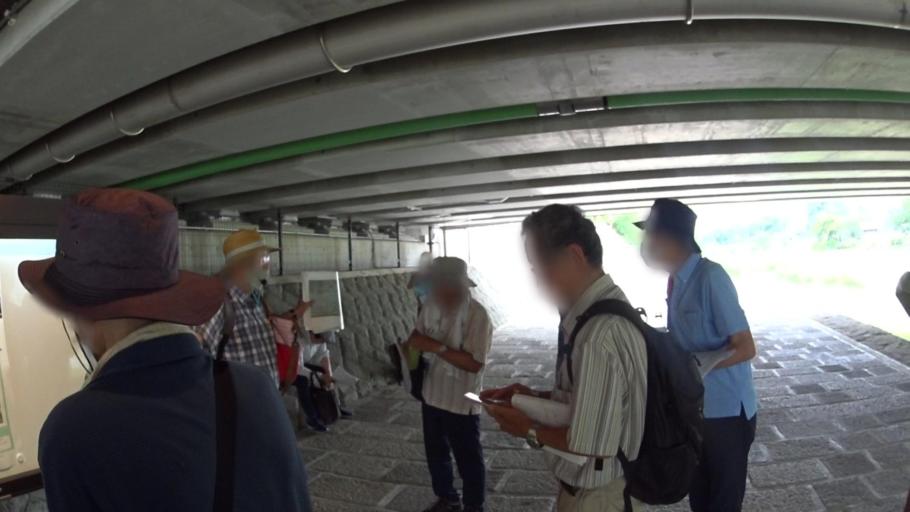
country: JP
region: Kyoto
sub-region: Kyoto-shi
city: Kamigyo-ku
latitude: 35.0561
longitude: 135.7526
